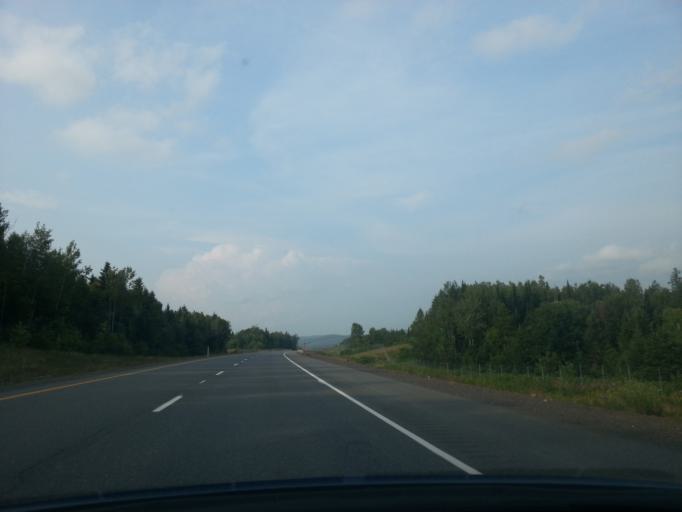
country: US
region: Maine
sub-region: Aroostook County
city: Fort Fairfield
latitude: 46.6497
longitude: -67.7406
